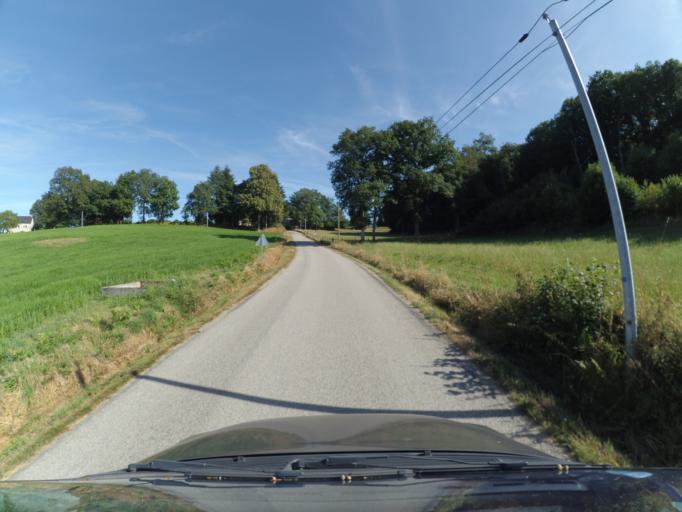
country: FR
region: Limousin
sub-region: Departement de la Correze
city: Bugeat
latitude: 45.6932
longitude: 1.8839
